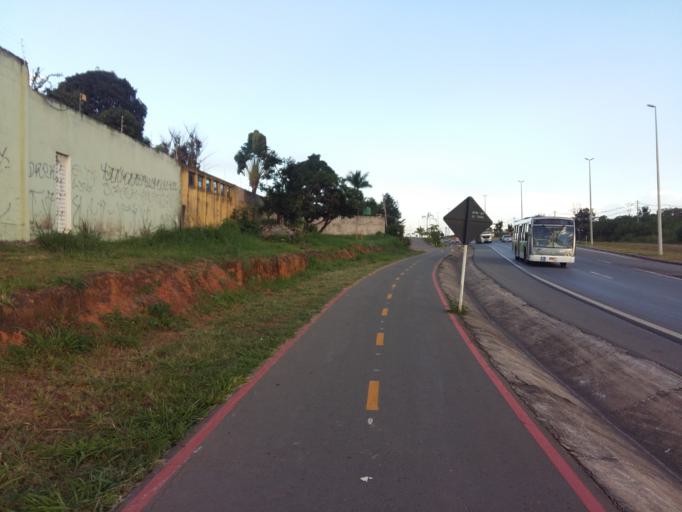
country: BR
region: Federal District
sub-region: Brasilia
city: Brasilia
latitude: -15.6407
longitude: -47.8492
